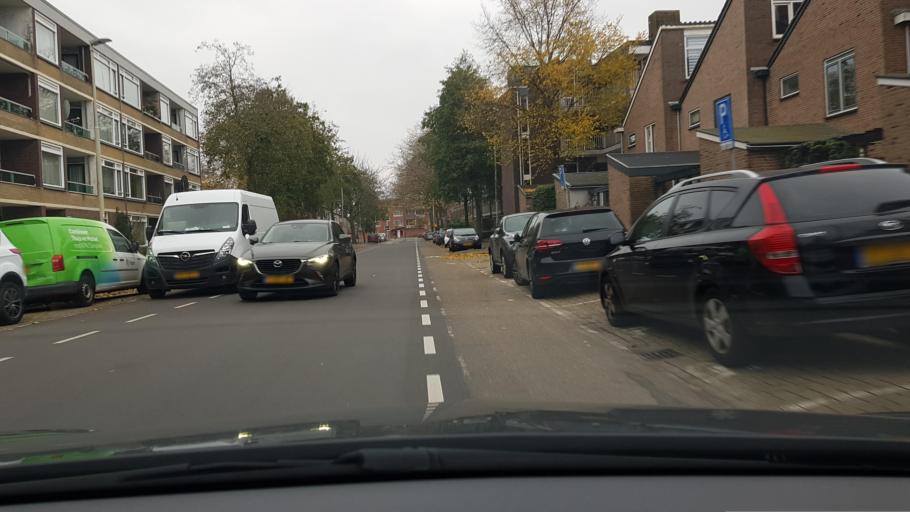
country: NL
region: North Holland
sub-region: Gemeente Haarlem
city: Haarlem
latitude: 52.3574
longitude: 4.6615
